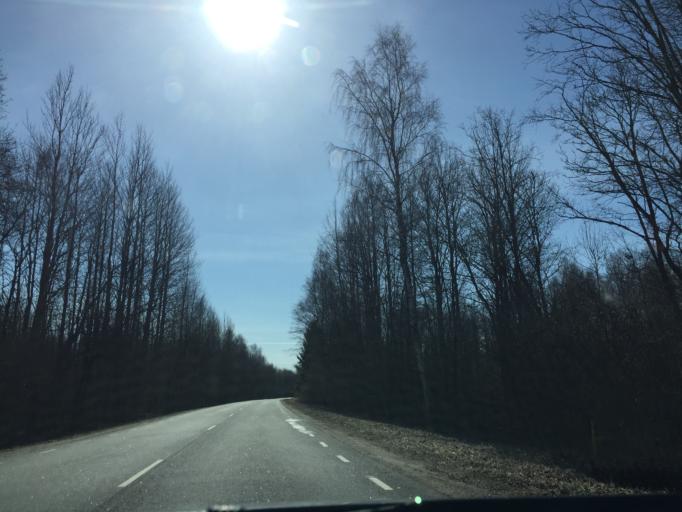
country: EE
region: Laeaene
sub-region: Lihula vald
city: Lihula
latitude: 58.6245
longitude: 23.6892
